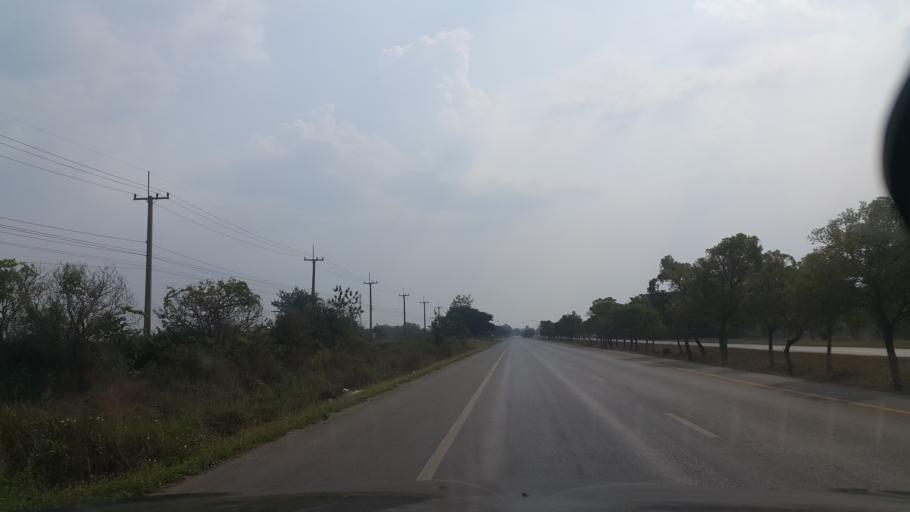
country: TH
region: Sukhothai
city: Sukhothai
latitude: 17.0617
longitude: 99.8868
